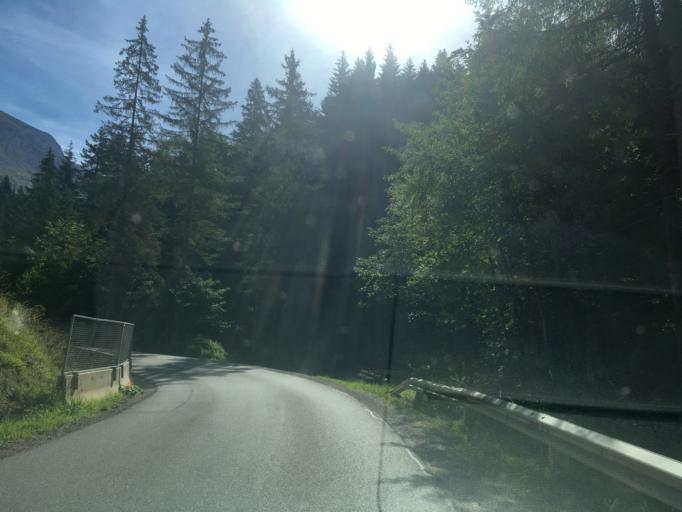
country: AT
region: Salzburg
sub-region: Politischer Bezirk Hallein
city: Abtenau
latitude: 47.5238
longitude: 13.4404
